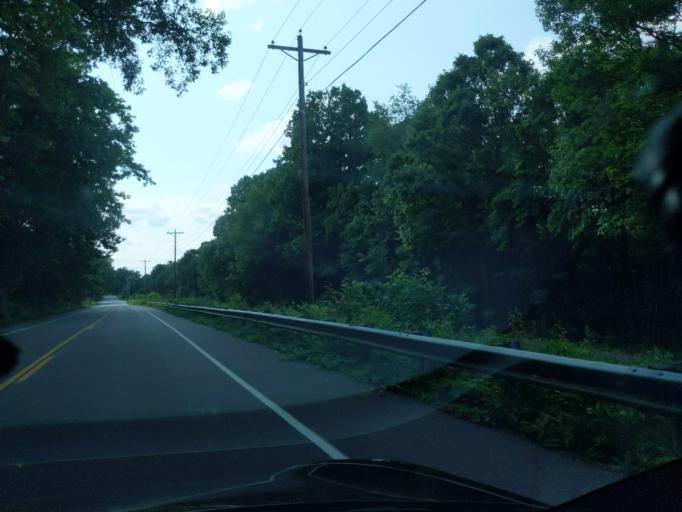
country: US
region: Michigan
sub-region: Kent County
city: Lowell
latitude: 42.9217
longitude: -85.3659
